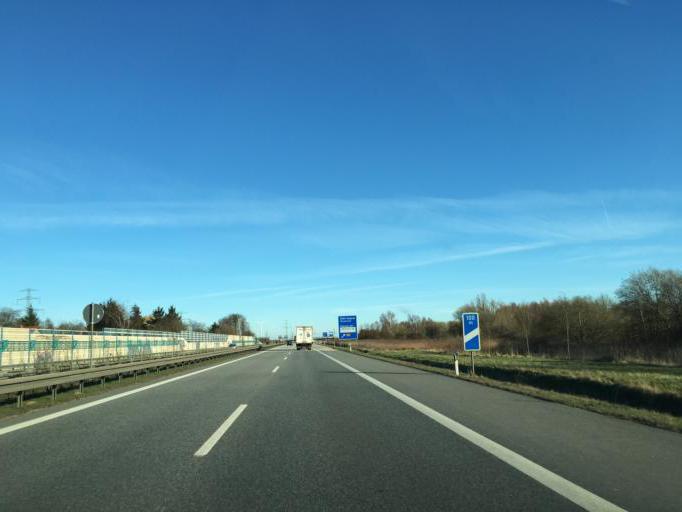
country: DE
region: Mecklenburg-Vorpommern
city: Dierkow-Neu
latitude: 54.1116
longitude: 12.1793
